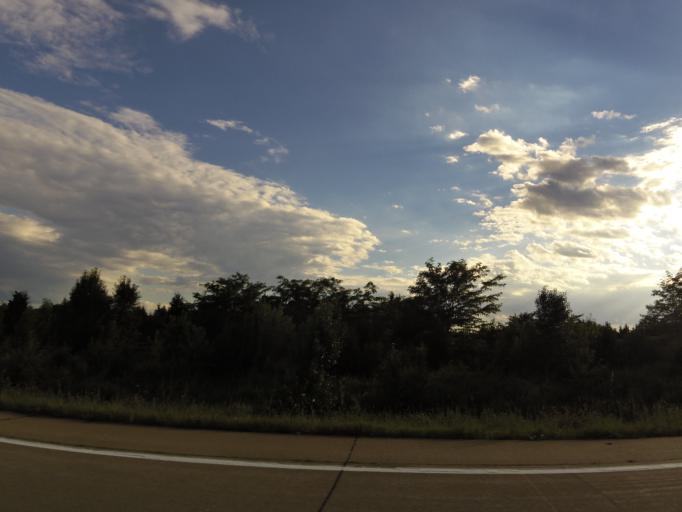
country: US
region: Missouri
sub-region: Saint Charles County
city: Dardenne Prairie
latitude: 38.7531
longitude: -90.7575
